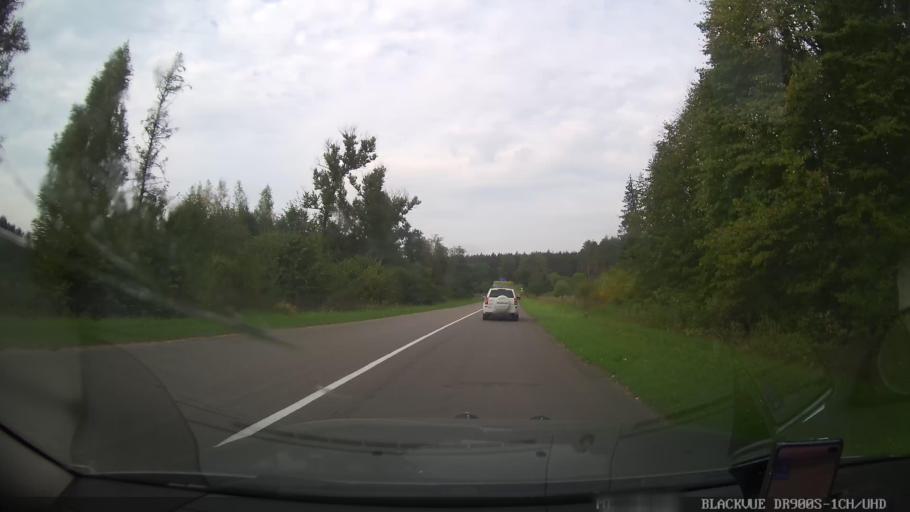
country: LT
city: Skaidiskes
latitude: 54.5888
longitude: 25.5564
